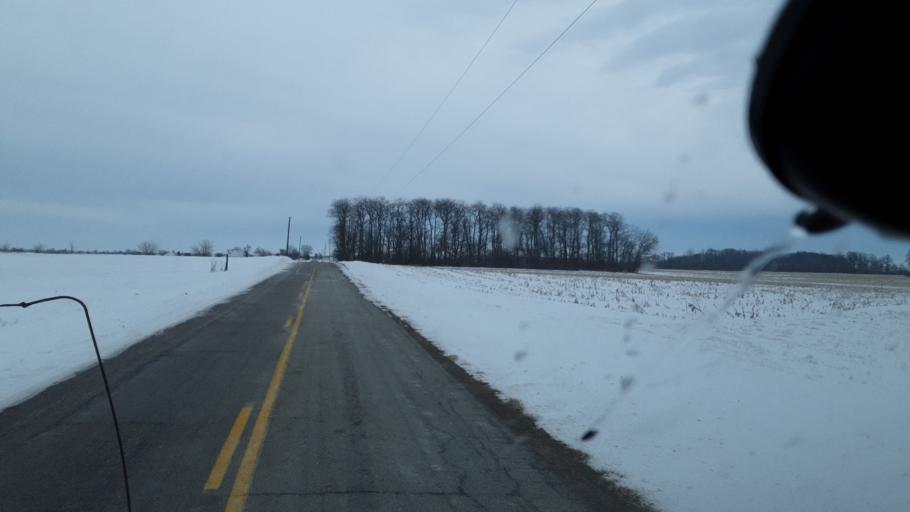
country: US
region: Ohio
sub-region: Madison County
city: Bethel
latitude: 39.7122
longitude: -83.3590
